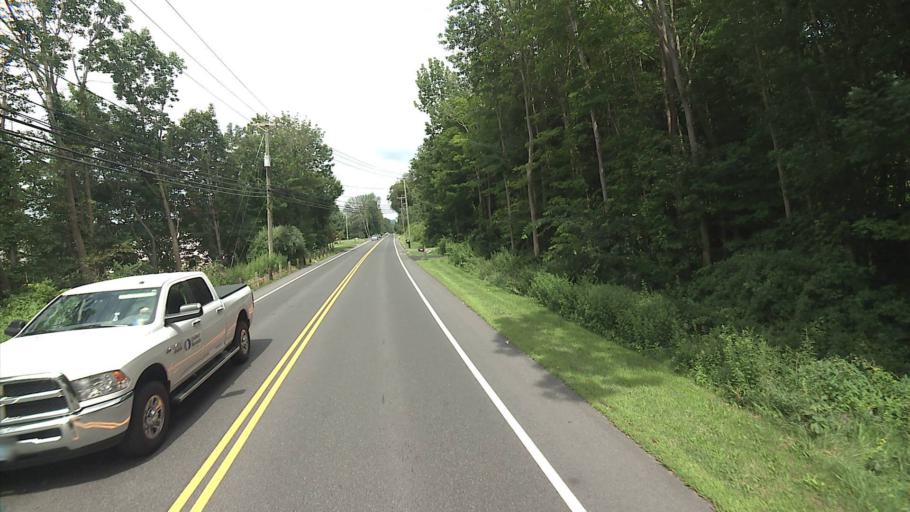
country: US
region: Connecticut
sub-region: New Haven County
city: Southbury
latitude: 41.4720
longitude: -73.1841
